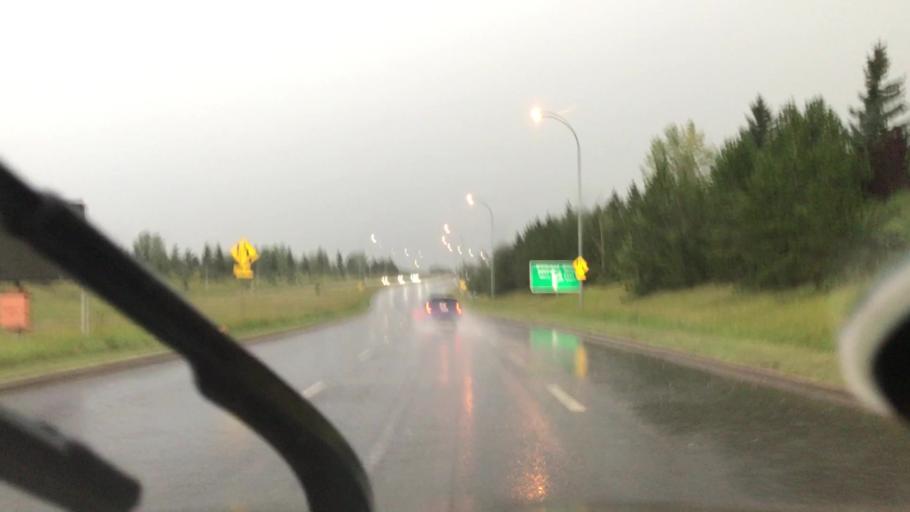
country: CA
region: Alberta
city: Edmonton
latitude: 53.4770
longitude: -113.5738
